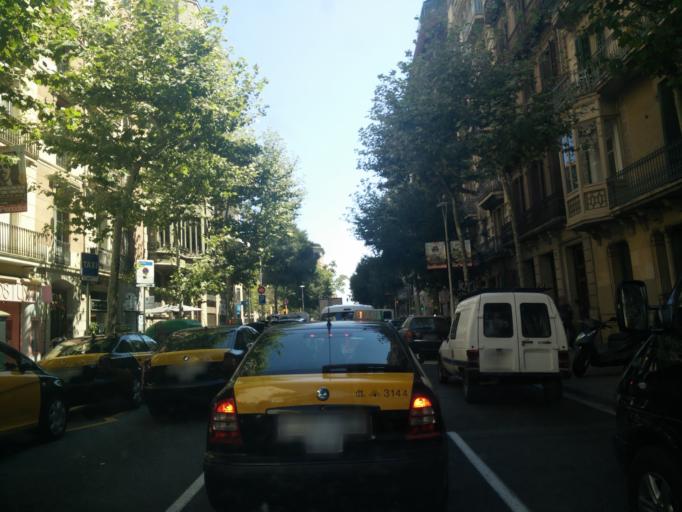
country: ES
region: Catalonia
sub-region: Provincia de Barcelona
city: Eixample
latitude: 41.3963
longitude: 2.1613
